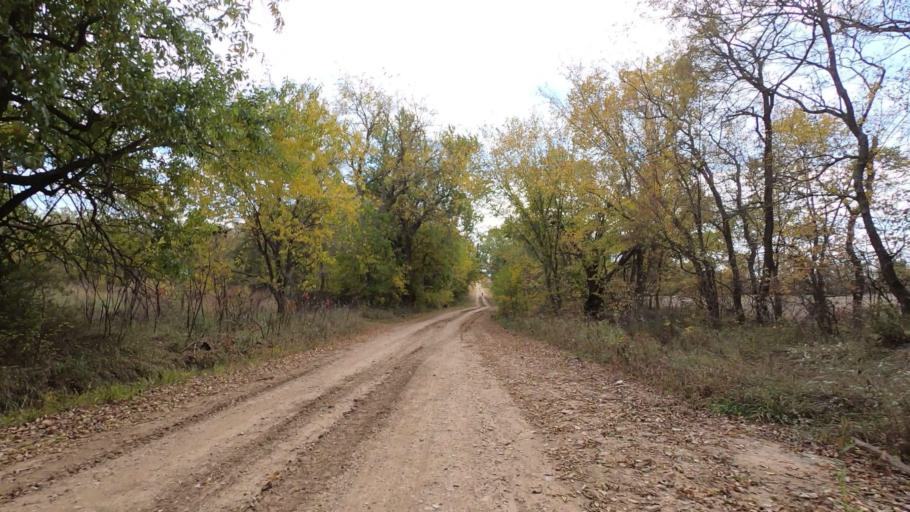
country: US
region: Kansas
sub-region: Pottawatomie County
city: Westmoreland
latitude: 39.3285
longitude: -96.4453
